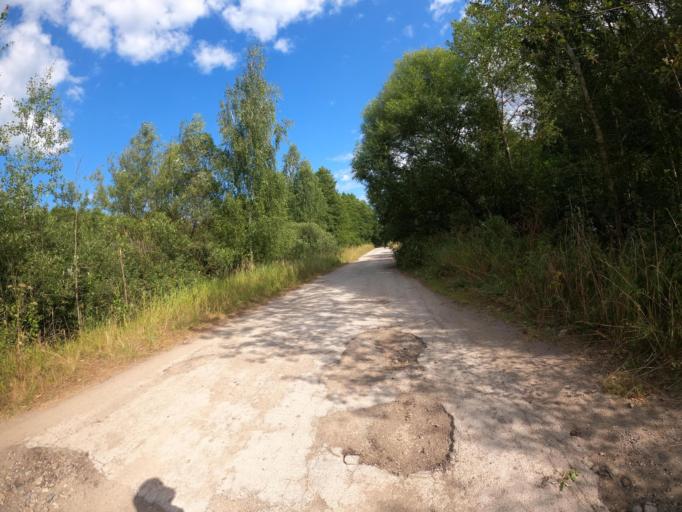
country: RU
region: Moskovskaya
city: Konobeyevo
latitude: 55.3845
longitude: 38.7016
